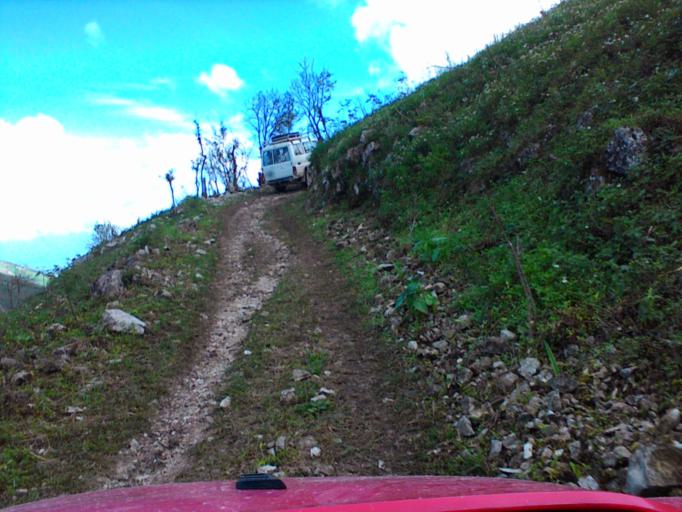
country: HT
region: Grandans
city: Moron
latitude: 18.4640
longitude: -74.1129
